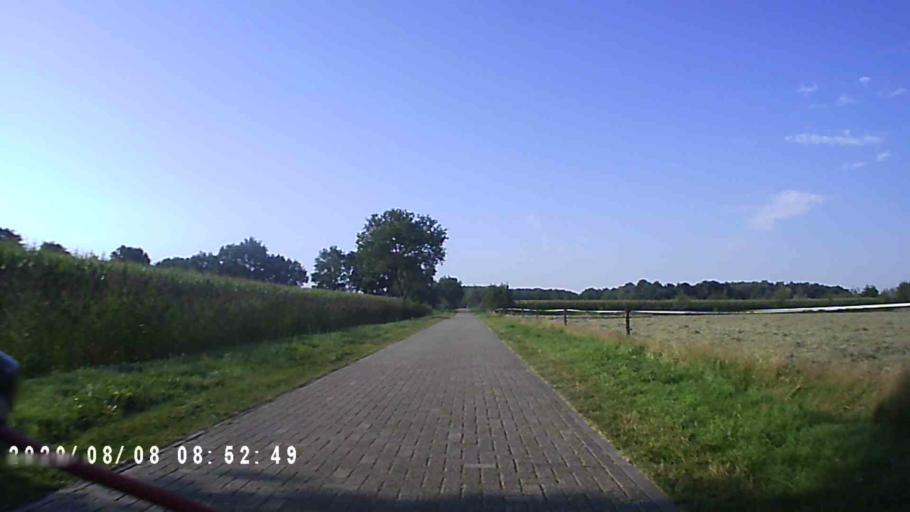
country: NL
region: Groningen
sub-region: Gemeente Leek
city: Leek
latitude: 53.0637
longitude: 6.3260
